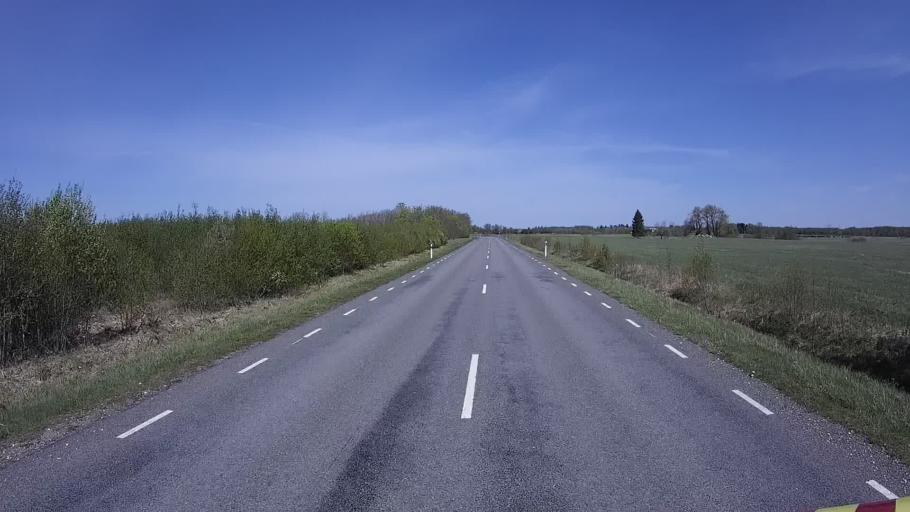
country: EE
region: Laeaene
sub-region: Lihula vald
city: Lihula
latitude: 58.6586
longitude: 23.8366
